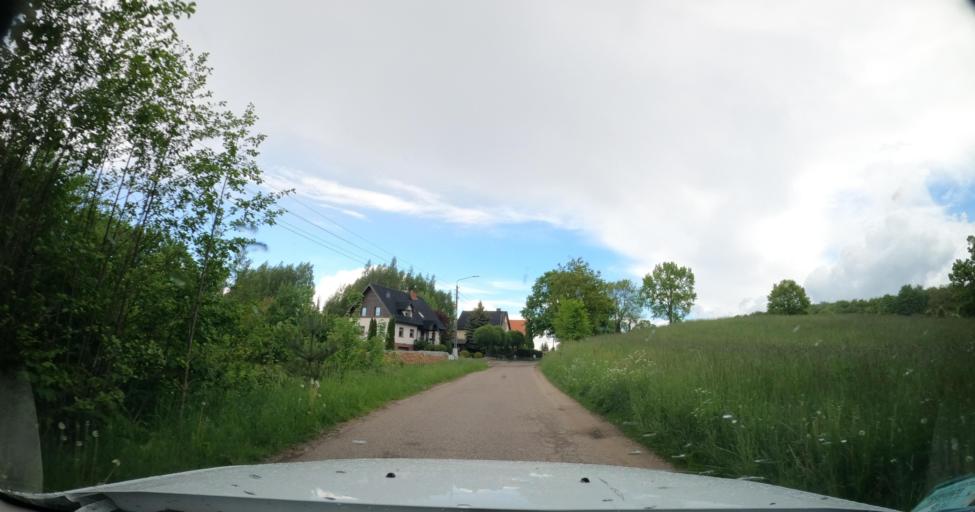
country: PL
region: Pomeranian Voivodeship
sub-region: Powiat kartuski
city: Garcz
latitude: 54.3407
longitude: 18.1453
